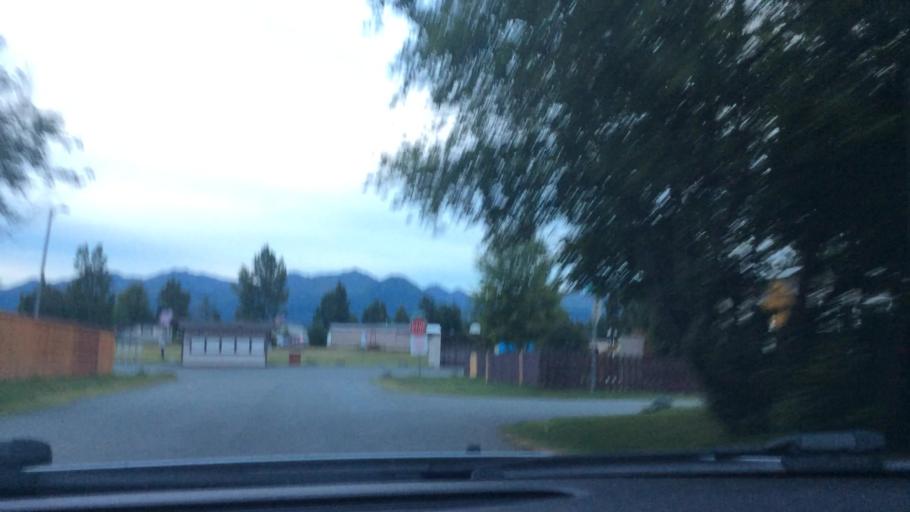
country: US
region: Alaska
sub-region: Anchorage Municipality
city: Anchorage
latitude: 61.1335
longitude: -149.8551
